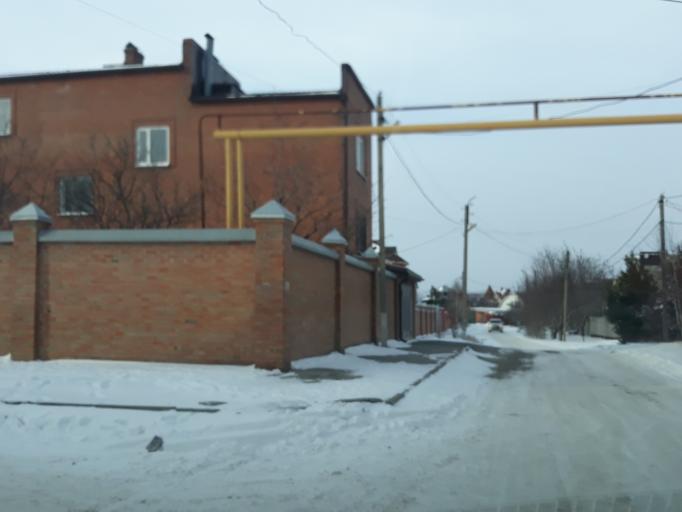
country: RU
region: Rostov
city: Novobessergenovka
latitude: 47.2242
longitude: 38.8421
